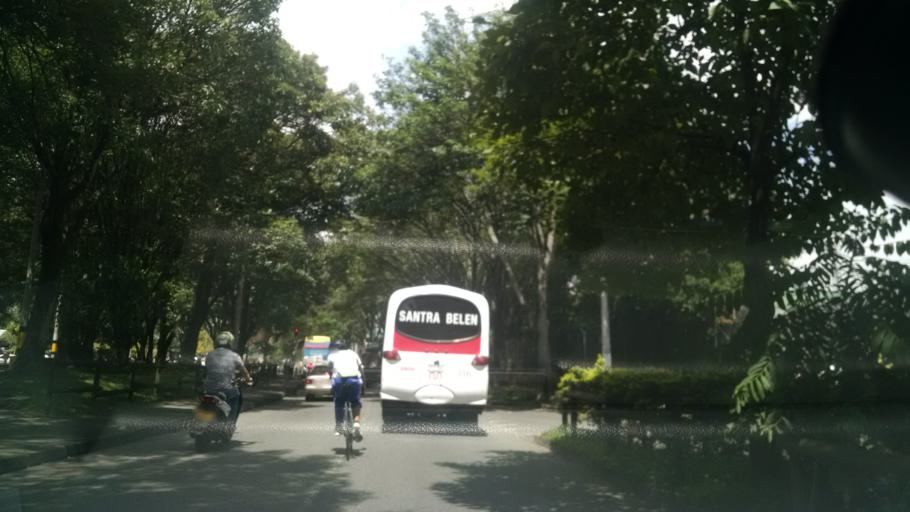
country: CO
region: Antioquia
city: Medellin
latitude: 6.2542
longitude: -75.5869
